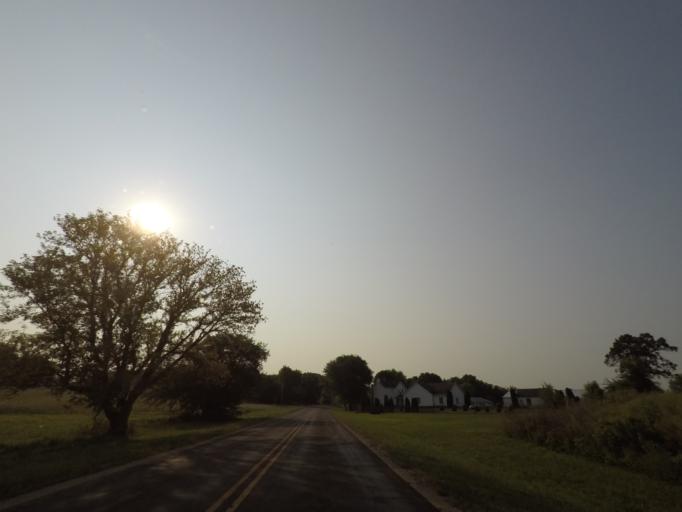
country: US
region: Wisconsin
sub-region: Dane County
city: Cottage Grove
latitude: 43.0431
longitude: -89.2312
